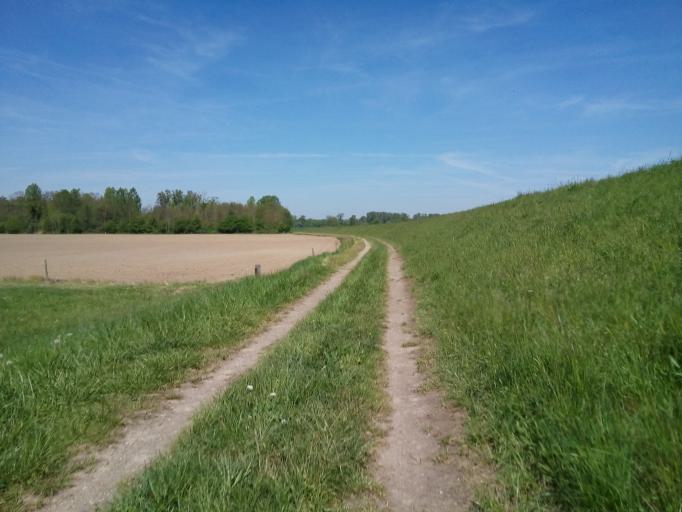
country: DE
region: Baden-Wuerttemberg
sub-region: Freiburg Region
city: Rheinau
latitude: 48.6931
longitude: 7.9709
